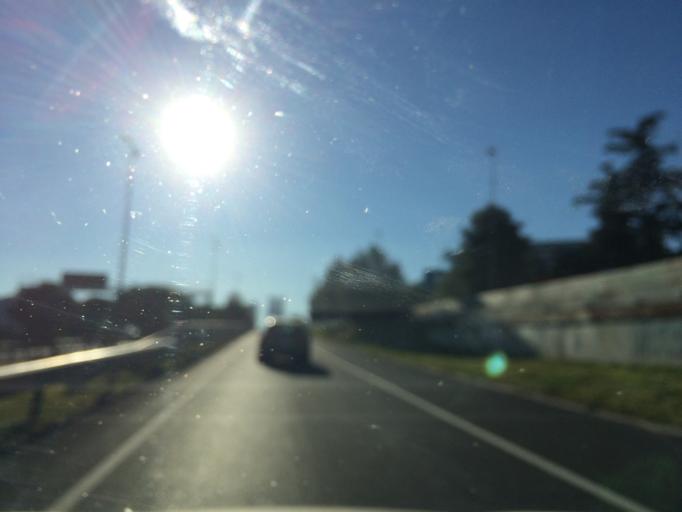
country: ES
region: Madrid
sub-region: Provincia de Madrid
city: Las Tablas
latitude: 40.4941
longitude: -3.6693
